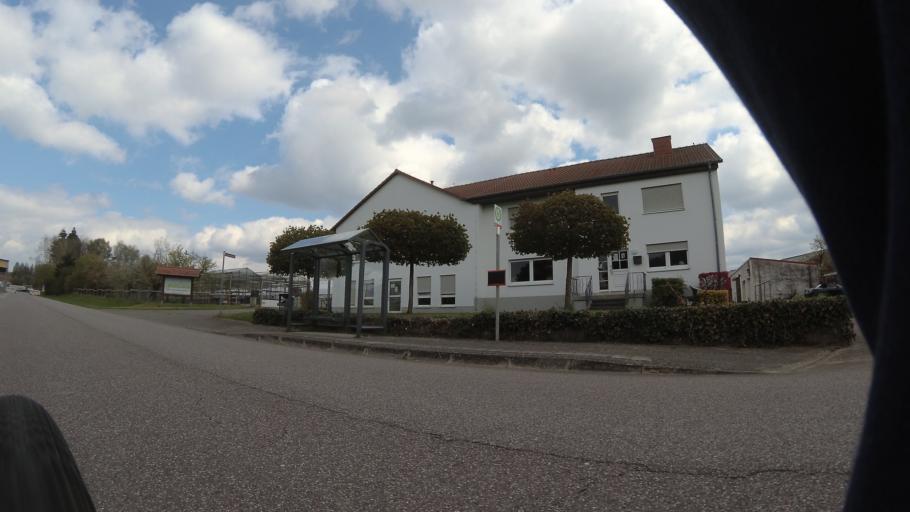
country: DE
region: Saarland
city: Weiskirchen
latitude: 49.4983
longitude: 6.8098
